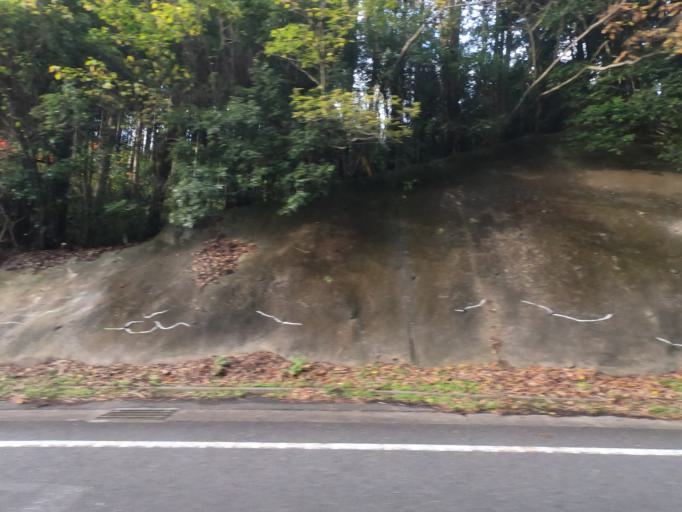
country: JP
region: Kumamoto
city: Minamata
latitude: 32.2453
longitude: 130.4708
